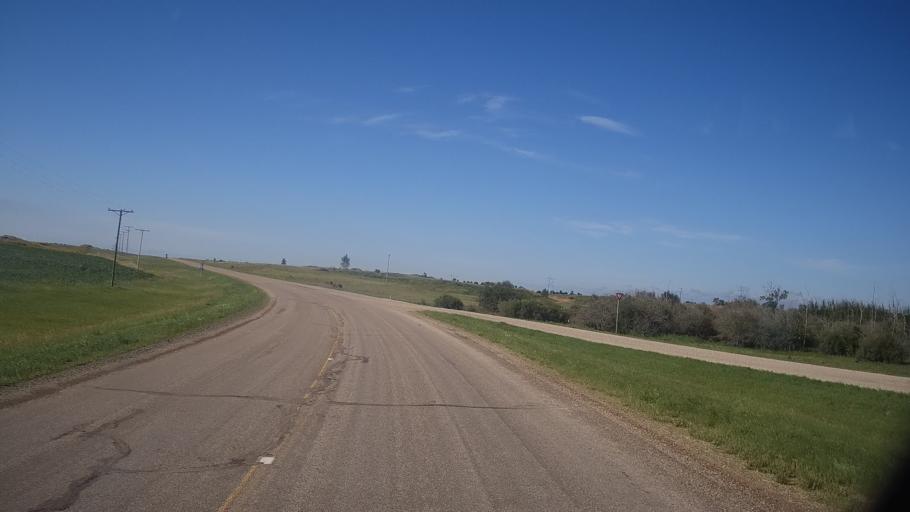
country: CA
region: Saskatchewan
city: Watrous
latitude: 51.7340
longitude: -105.3569
